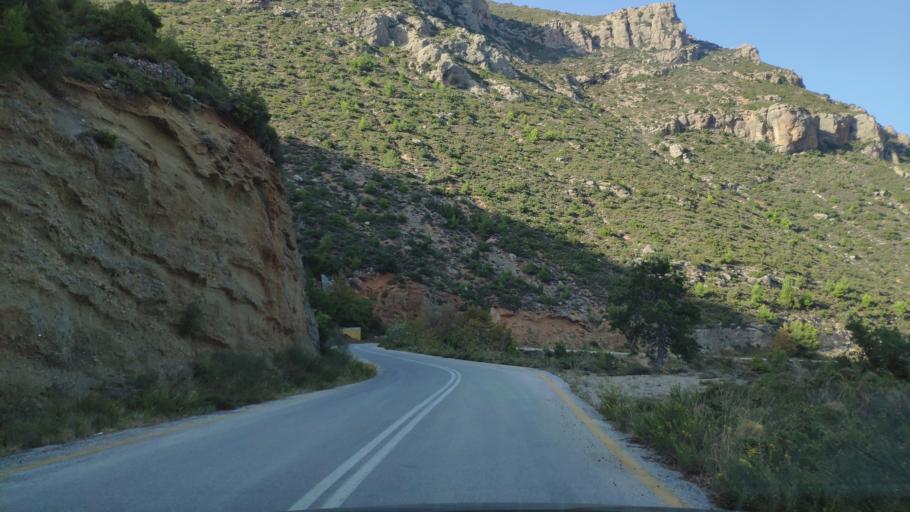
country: GR
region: West Greece
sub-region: Nomos Achaias
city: Aiyira
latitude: 38.0667
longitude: 22.3794
